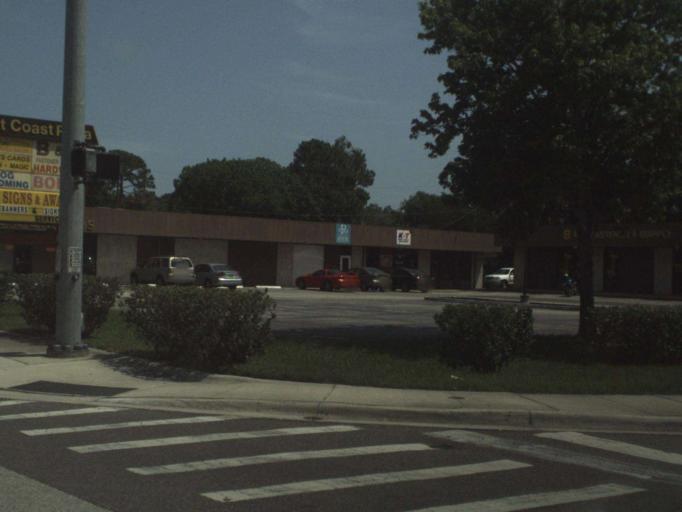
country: US
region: Florida
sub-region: Volusia County
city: Ormond Beach
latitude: 29.2752
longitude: -81.0580
